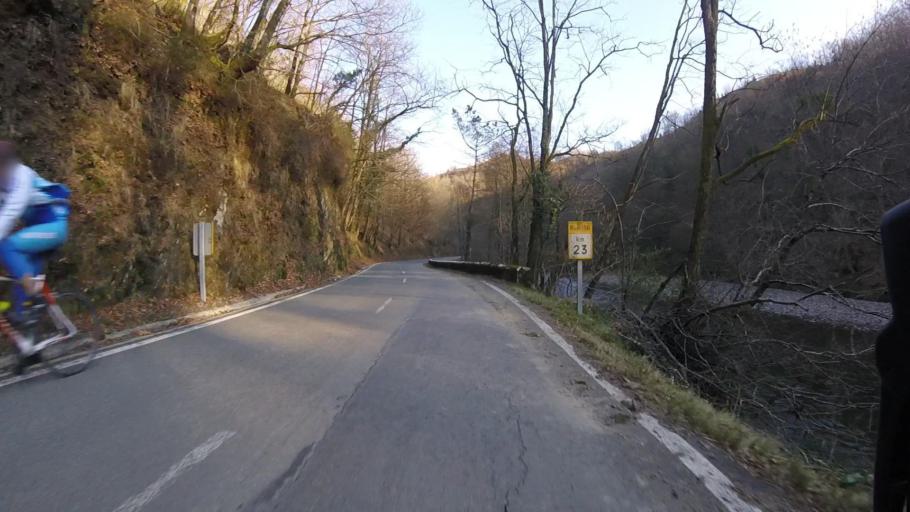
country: ES
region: Navarre
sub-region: Provincia de Navarra
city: Arano
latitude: 43.2095
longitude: -1.8788
